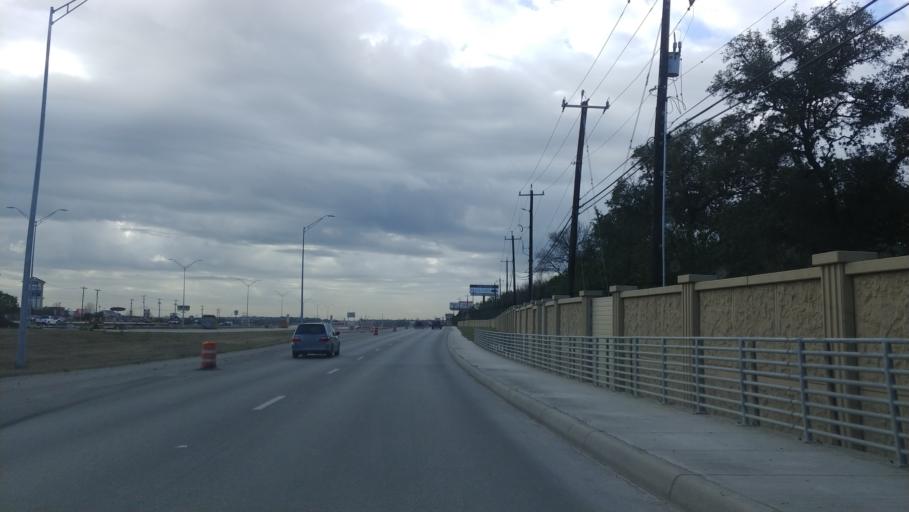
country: US
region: Texas
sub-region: Bexar County
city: Leon Valley
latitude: 29.4416
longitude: -98.7117
